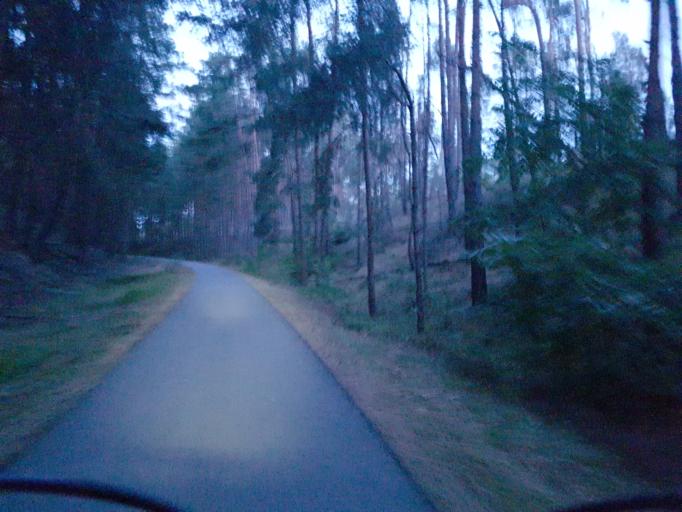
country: DE
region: Brandenburg
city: Trobitz
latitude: 51.5621
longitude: 13.4447
